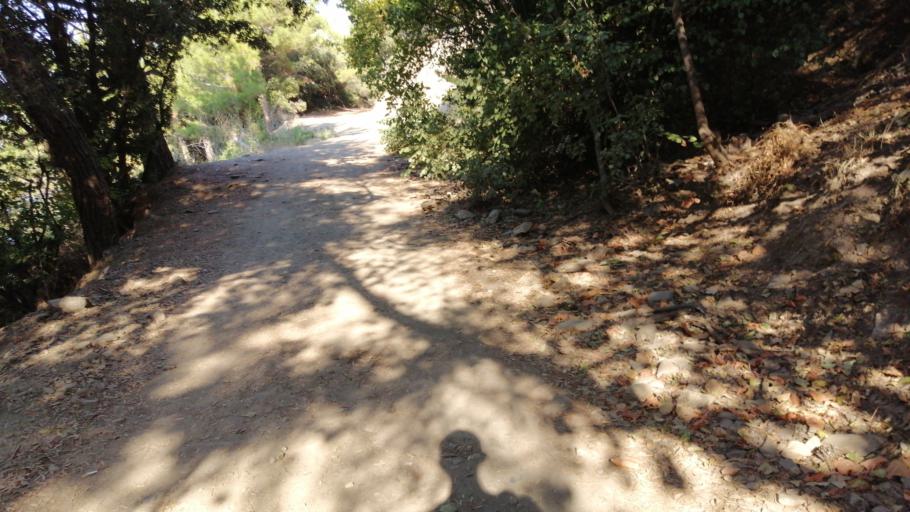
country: TR
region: Aydin
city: Atburgazi
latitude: 37.6902
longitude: 27.1356
